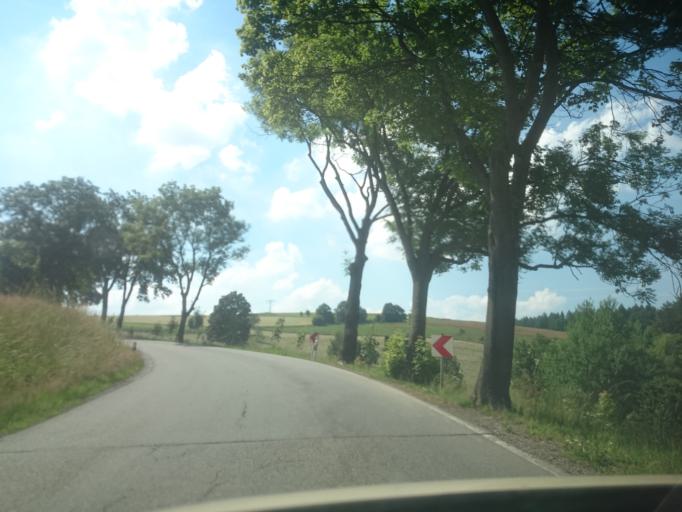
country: DE
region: Saxony
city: Pockau
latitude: 50.7121
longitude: 13.2145
